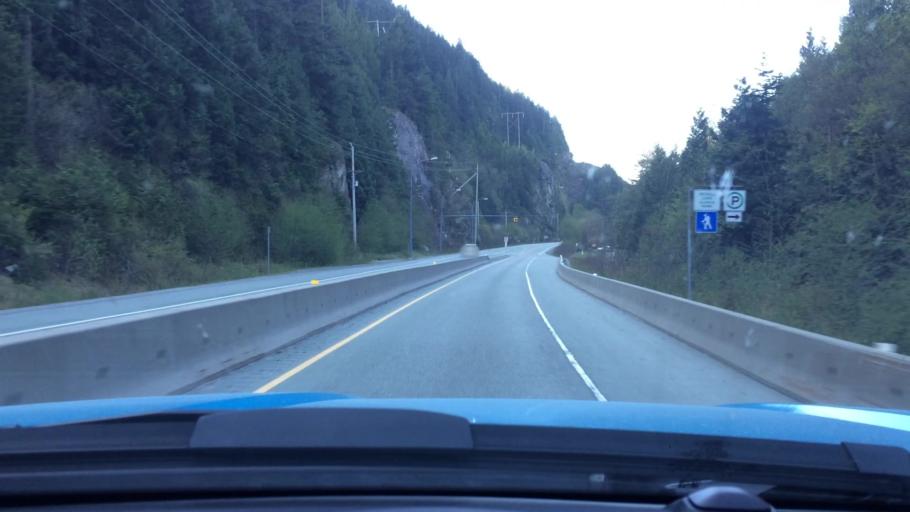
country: CA
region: British Columbia
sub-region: Greater Vancouver Regional District
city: Lions Bay
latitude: 49.6475
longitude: -123.2024
